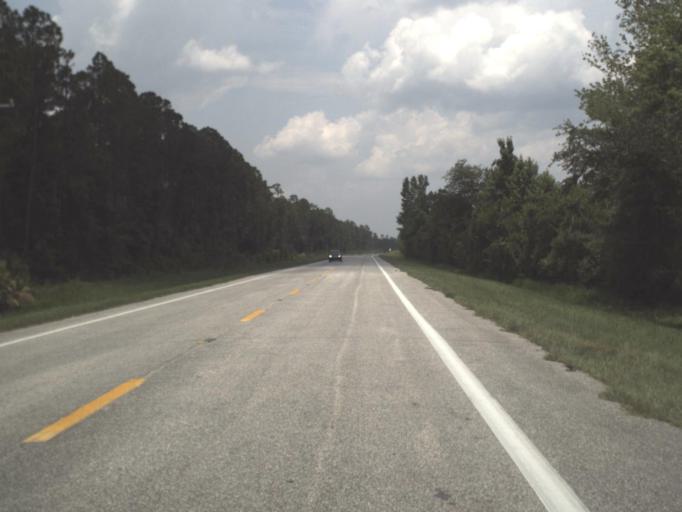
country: US
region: Florida
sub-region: Putnam County
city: Palatka
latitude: 29.5526
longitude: -81.7379
